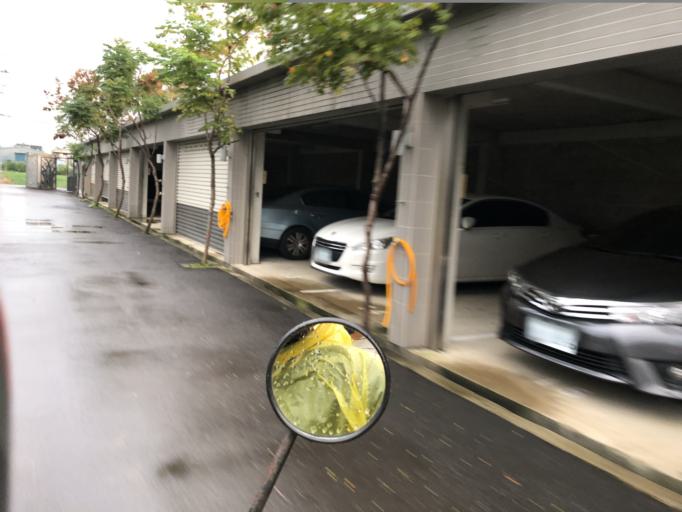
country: TW
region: Taiwan
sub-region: Hsinchu
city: Zhubei
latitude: 24.8515
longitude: 120.9893
